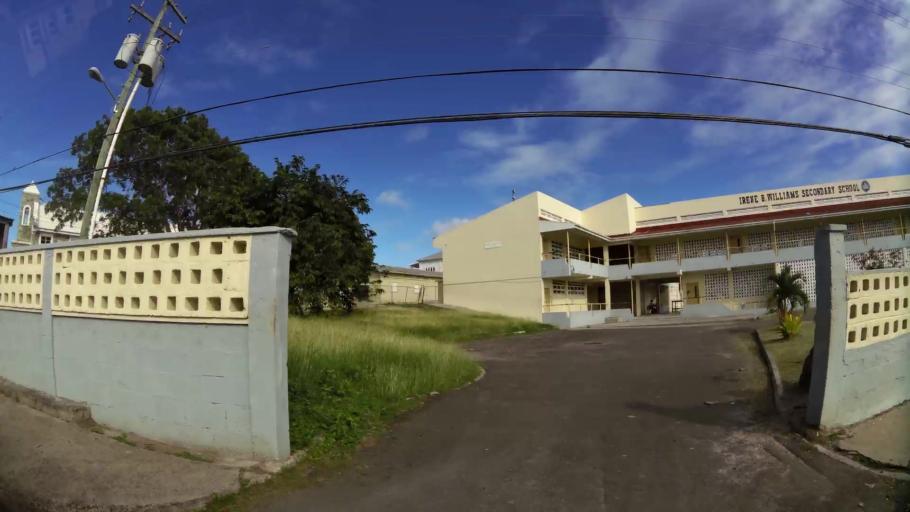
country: AG
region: Saint Peter
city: All Saints
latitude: 17.0514
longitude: -61.8013
